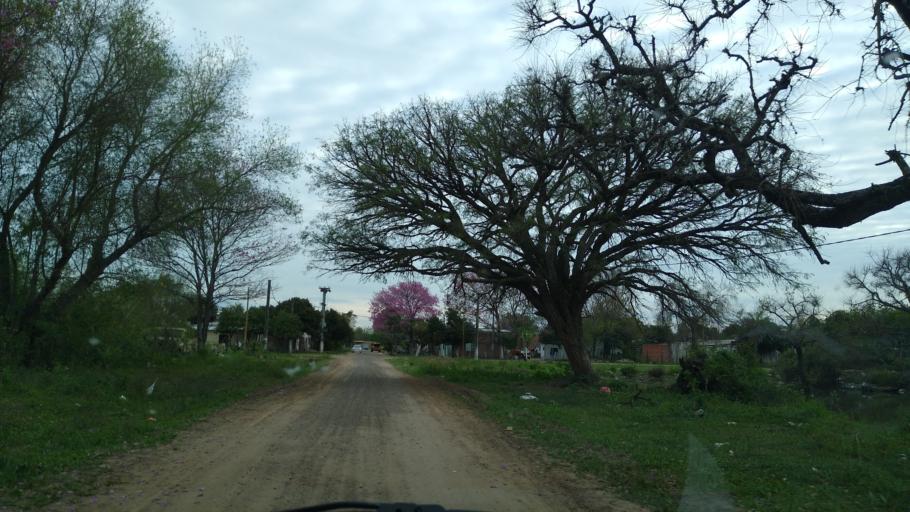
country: AR
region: Chaco
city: Fontana
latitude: -27.4005
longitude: -59.0389
